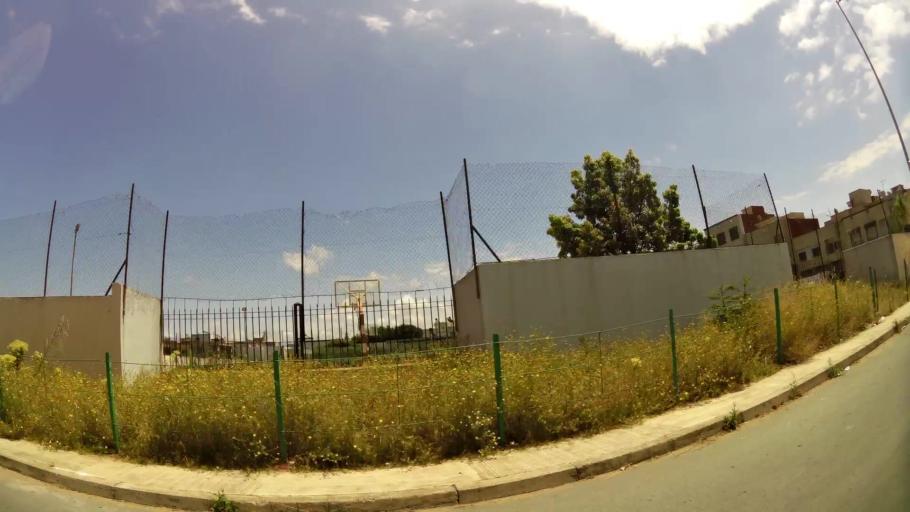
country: MA
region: Gharb-Chrarda-Beni Hssen
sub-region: Kenitra Province
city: Kenitra
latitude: 34.2702
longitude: -6.6171
